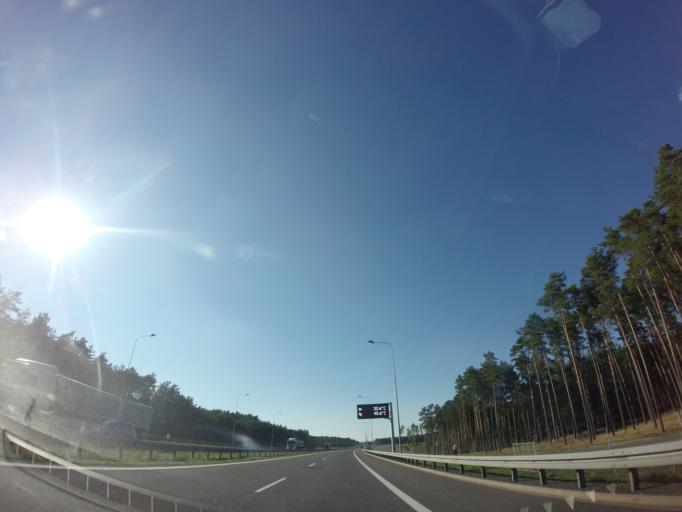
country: PL
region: Lubusz
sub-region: Powiat gorzowski
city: Deszczno
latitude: 52.6201
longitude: 15.3856
